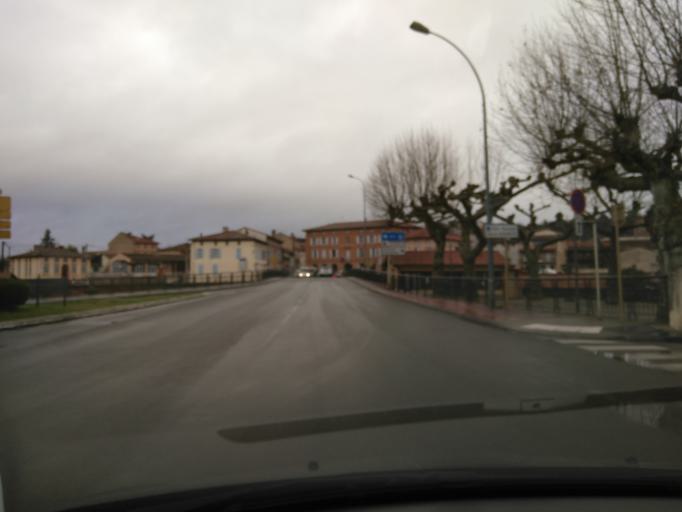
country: FR
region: Midi-Pyrenees
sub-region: Departement de la Haute-Garonne
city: Montesquieu-Volvestre
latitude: 43.2055
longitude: 1.2284
